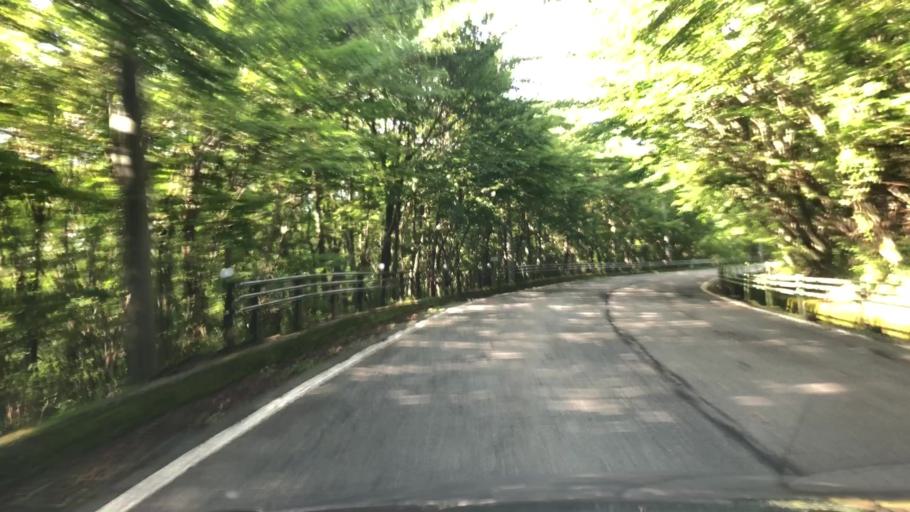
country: JP
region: Shizuoka
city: Gotemba
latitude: 35.3338
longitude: 138.8254
